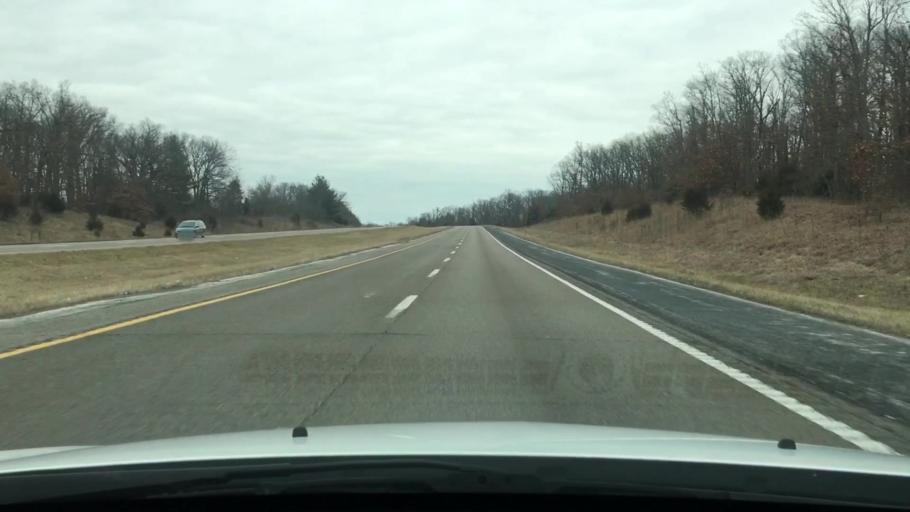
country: US
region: Missouri
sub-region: Callaway County
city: Fulton
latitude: 38.9726
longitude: -91.8970
